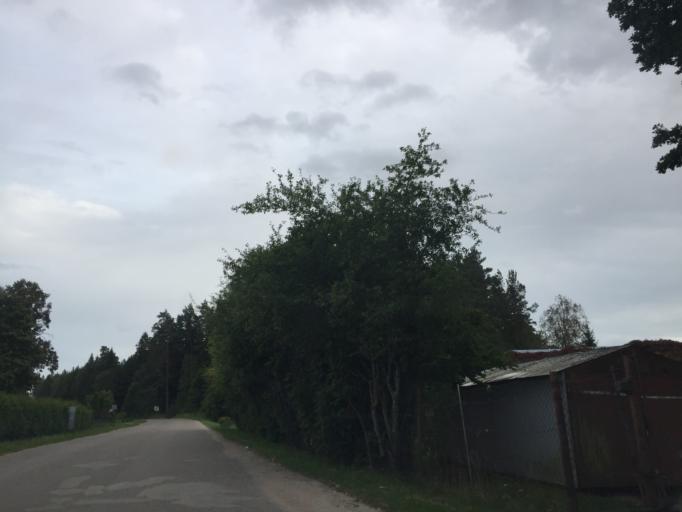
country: LV
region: Saulkrastu
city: Saulkrasti
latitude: 57.3345
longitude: 24.4298
